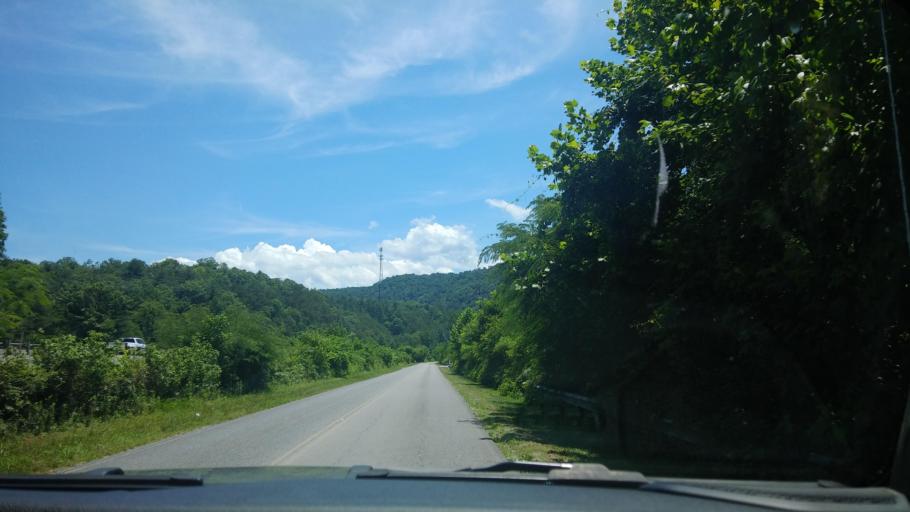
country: US
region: Tennessee
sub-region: Cocke County
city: Newport
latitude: 35.8208
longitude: -83.1514
